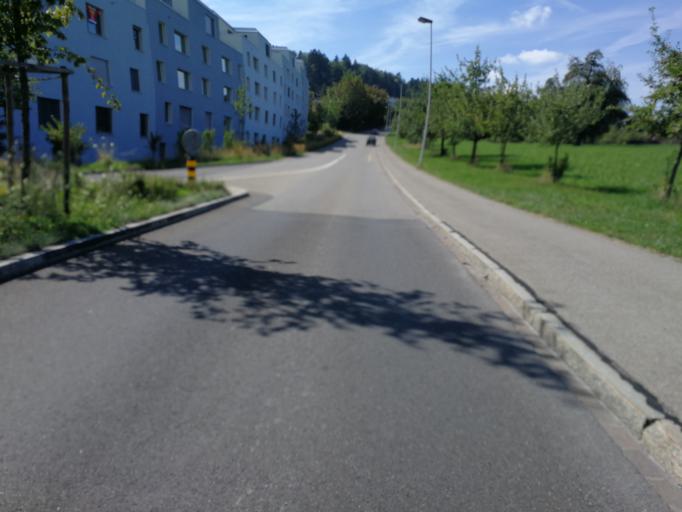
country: CH
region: Zurich
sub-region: Bezirk Horgen
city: Au
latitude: 47.2417
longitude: 8.6452
